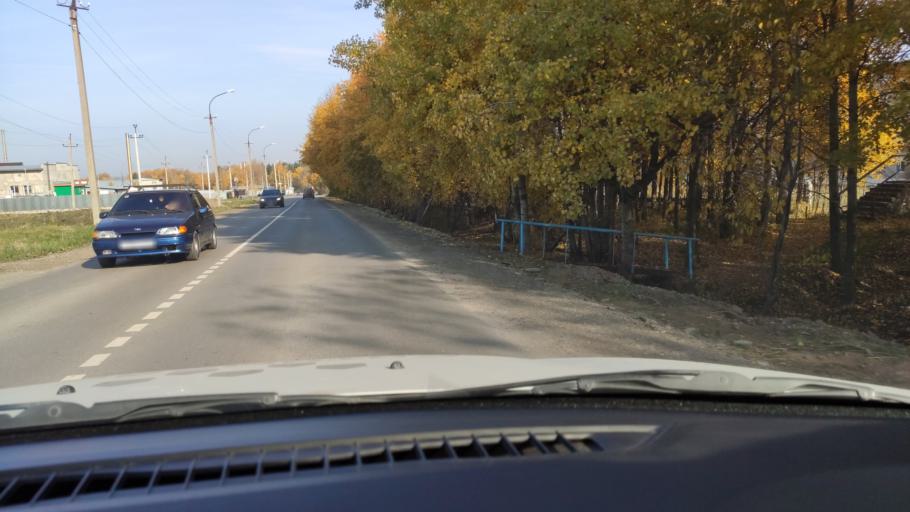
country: RU
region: Perm
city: Sylva
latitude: 58.0274
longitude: 56.7392
